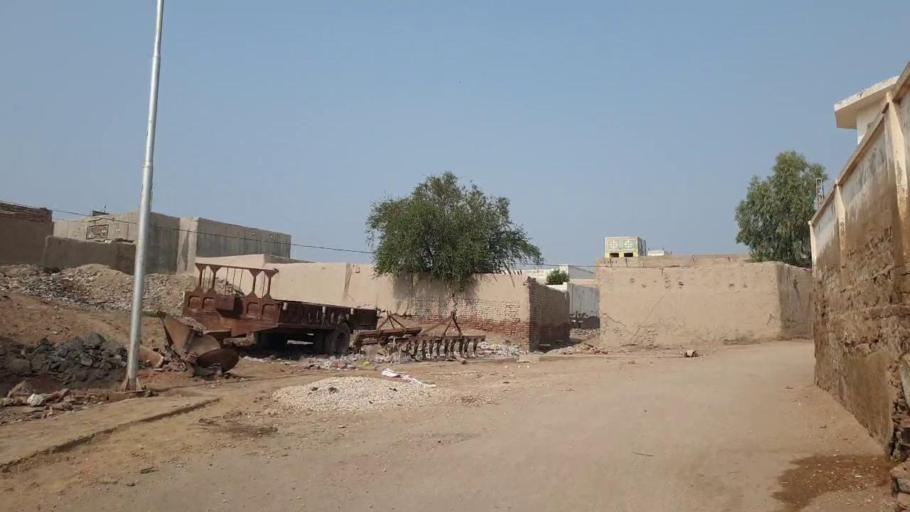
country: PK
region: Sindh
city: Bhan
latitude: 26.4453
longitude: 67.7200
